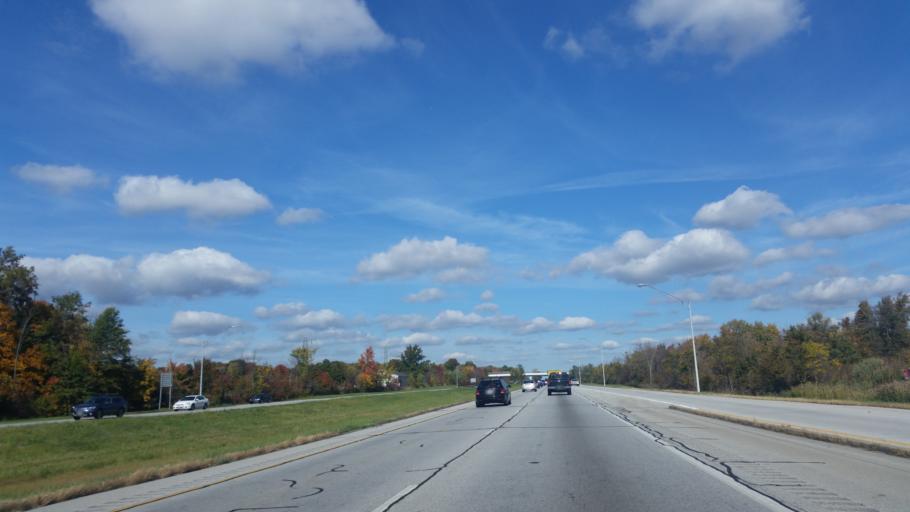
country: US
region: Ohio
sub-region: Summit County
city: Richfield
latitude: 41.1971
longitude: -81.6255
